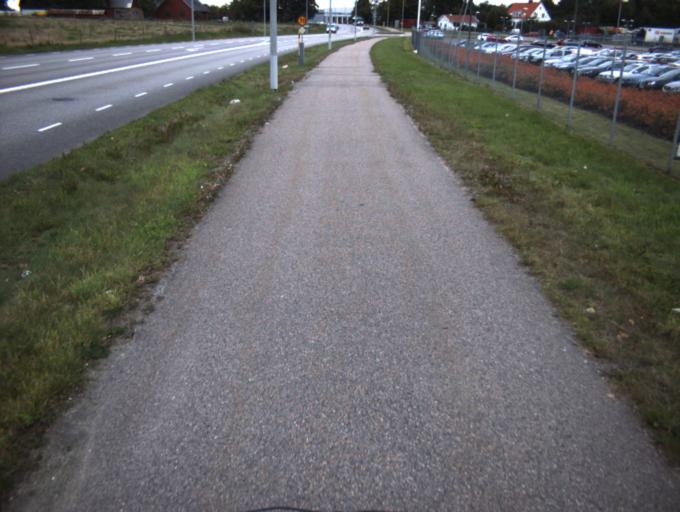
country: SE
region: Skane
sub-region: Helsingborg
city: Barslov
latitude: 56.0390
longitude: 12.7798
